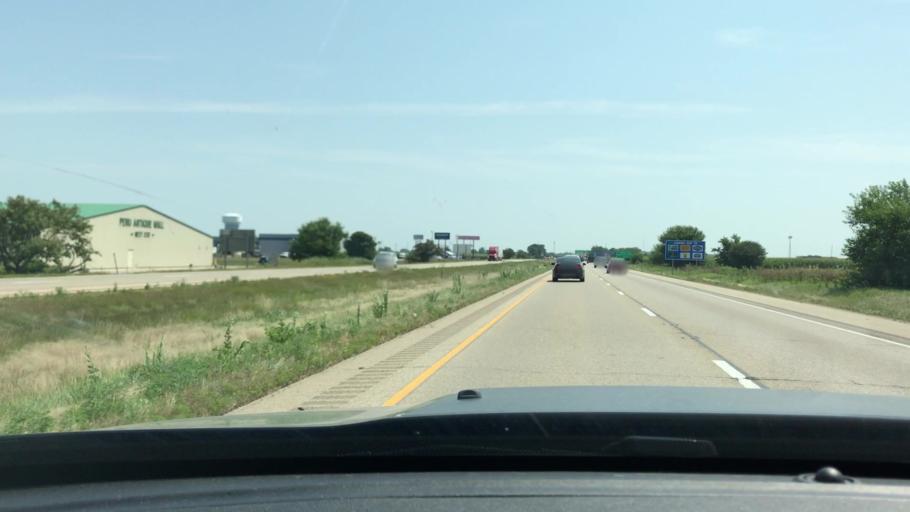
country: US
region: Illinois
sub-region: LaSalle County
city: Peru
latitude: 41.3649
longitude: -89.1419
